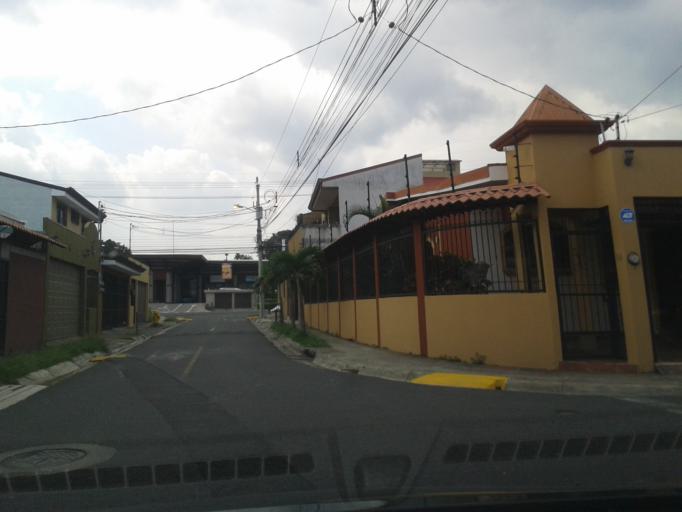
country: CR
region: Heredia
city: San Francisco
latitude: 9.9904
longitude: -84.1338
